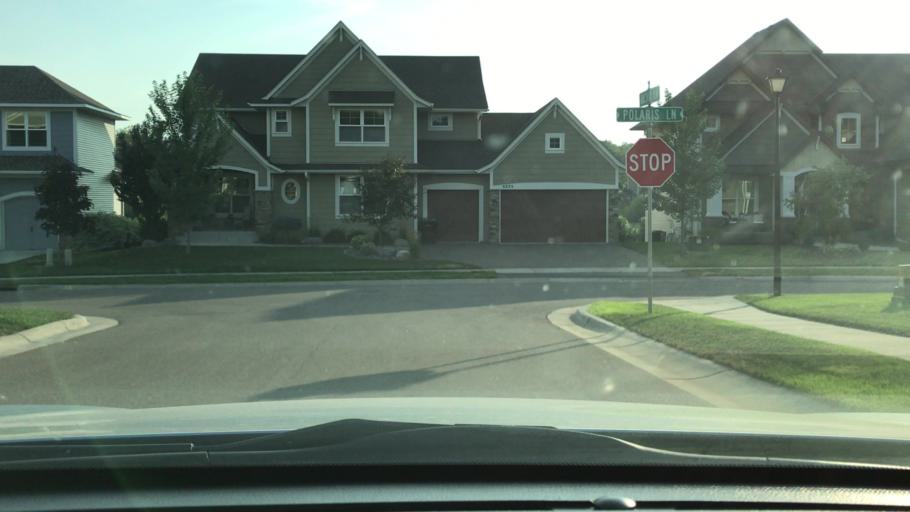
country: US
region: Minnesota
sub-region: Hennepin County
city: Maple Grove
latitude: 45.0522
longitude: -93.4734
